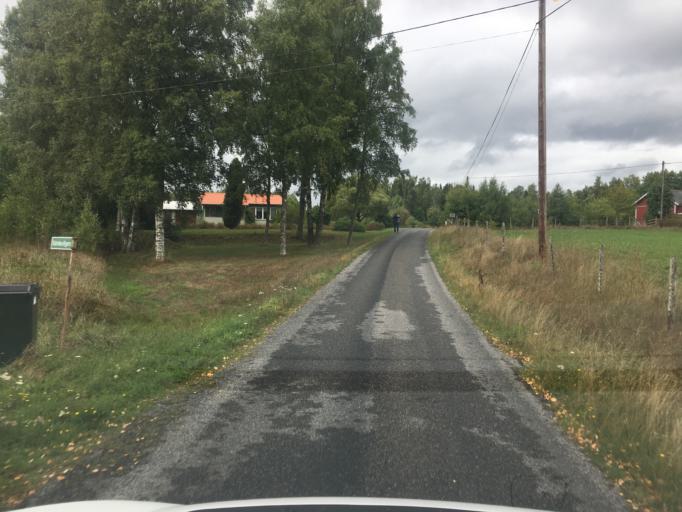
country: SE
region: Kronoberg
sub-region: Ljungby Kommun
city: Lagan
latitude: 56.9324
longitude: 14.0254
